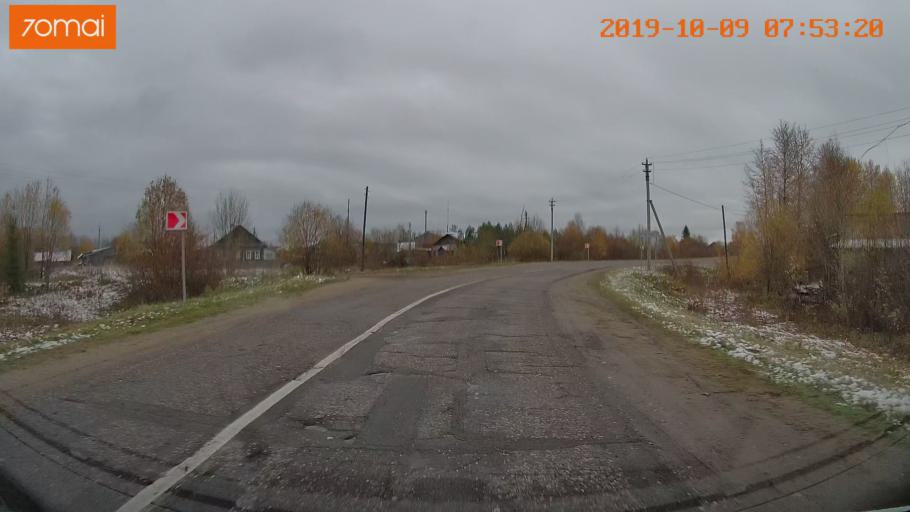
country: RU
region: Jaroslavl
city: Kukoboy
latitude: 58.6977
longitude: 39.8941
